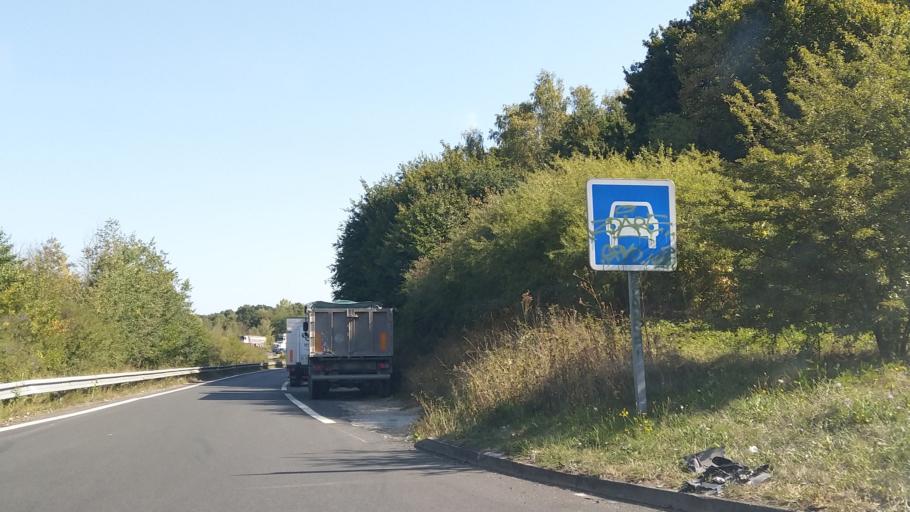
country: FR
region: Ile-de-France
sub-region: Departement du Val-d'Oise
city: Meriel
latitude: 49.0699
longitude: 2.2214
